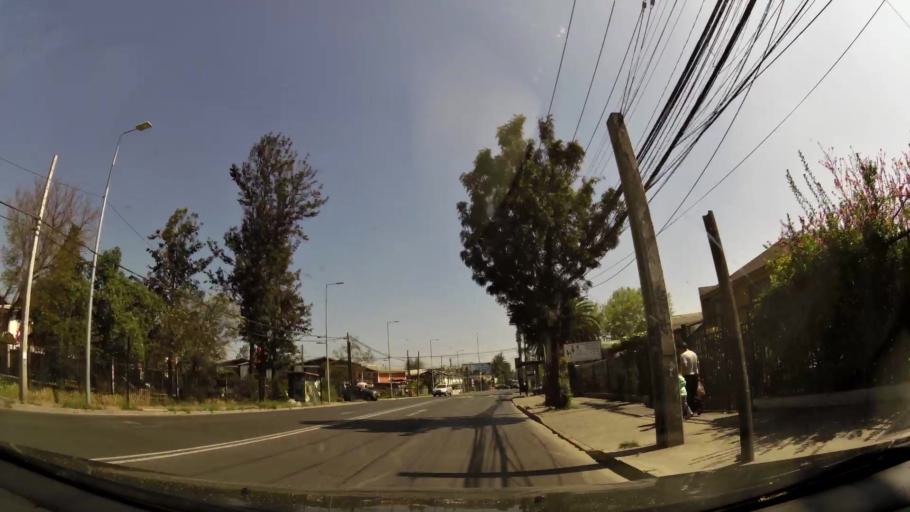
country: CL
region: Santiago Metropolitan
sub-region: Provincia de Santiago
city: Lo Prado
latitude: -33.3663
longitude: -70.7234
